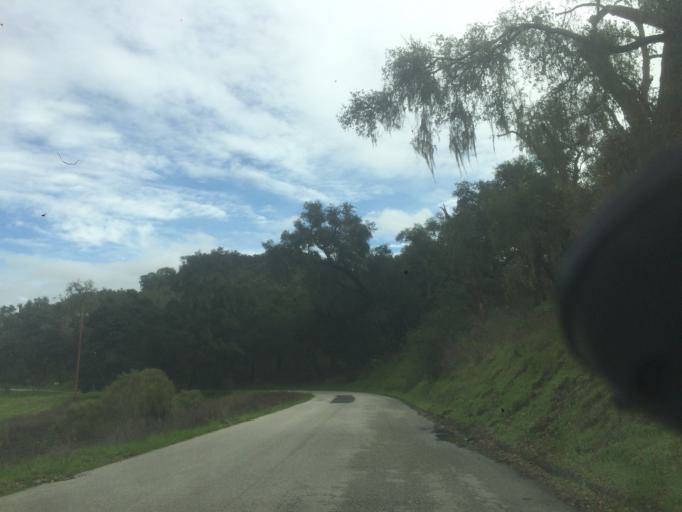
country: US
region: California
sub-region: San Luis Obispo County
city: Nipomo
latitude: 35.2061
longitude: -120.4167
